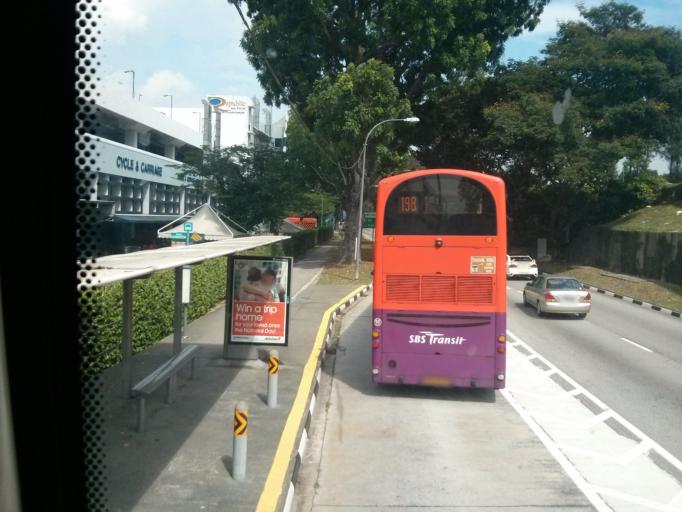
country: SG
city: Singapore
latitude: 1.3226
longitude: 103.7477
